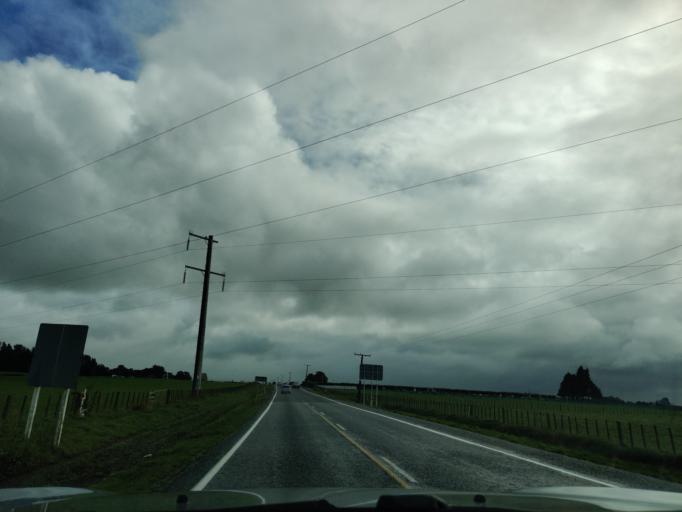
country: NZ
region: Hawke's Bay
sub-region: Hastings District
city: Hastings
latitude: -40.0209
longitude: 176.3216
